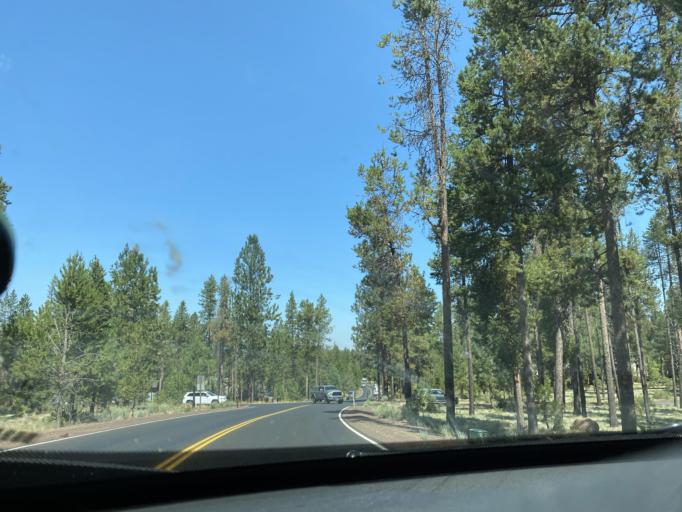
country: US
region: Oregon
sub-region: Deschutes County
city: Sunriver
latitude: 43.8945
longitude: -121.4170
